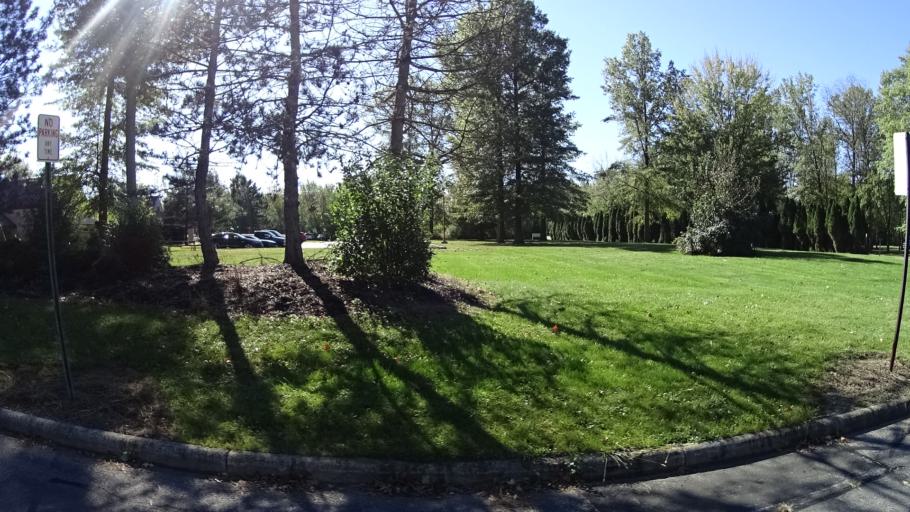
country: US
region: Ohio
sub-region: Lorain County
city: Oberlin
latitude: 41.3002
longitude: -82.2030
